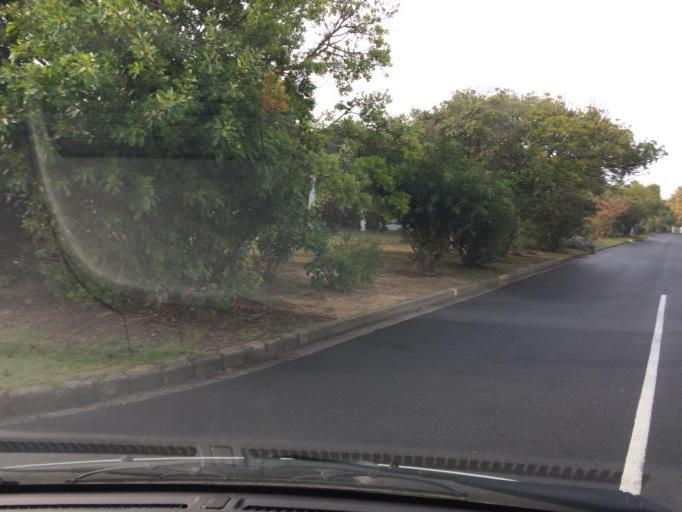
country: ZA
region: Western Cape
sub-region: City of Cape Town
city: Kraaifontein
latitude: -33.8599
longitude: 18.6459
